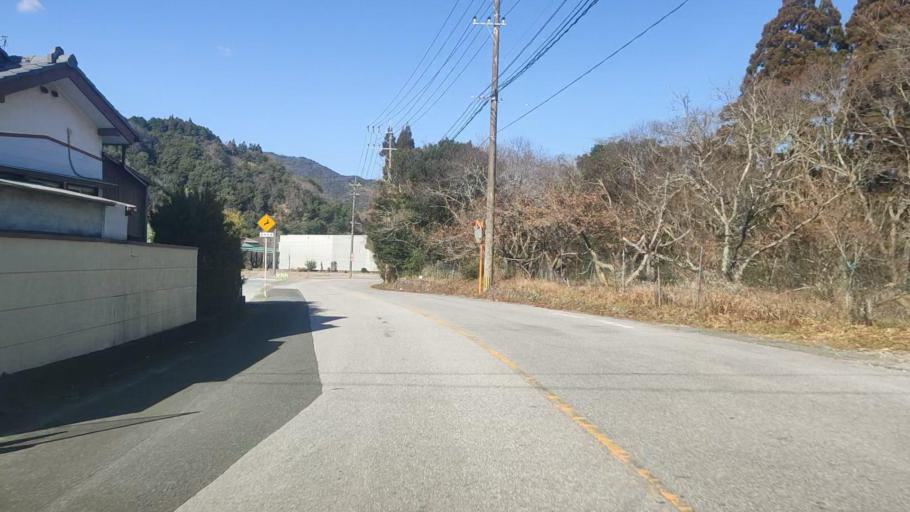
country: JP
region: Oita
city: Saiki
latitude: 32.9041
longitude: 131.9330
